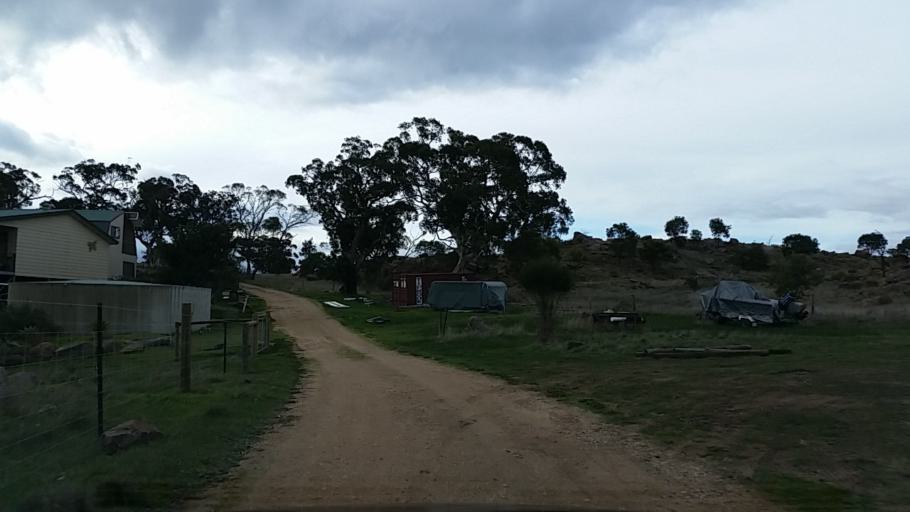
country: AU
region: South Australia
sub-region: Mount Barker
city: Callington
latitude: -34.9555
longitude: 139.0580
